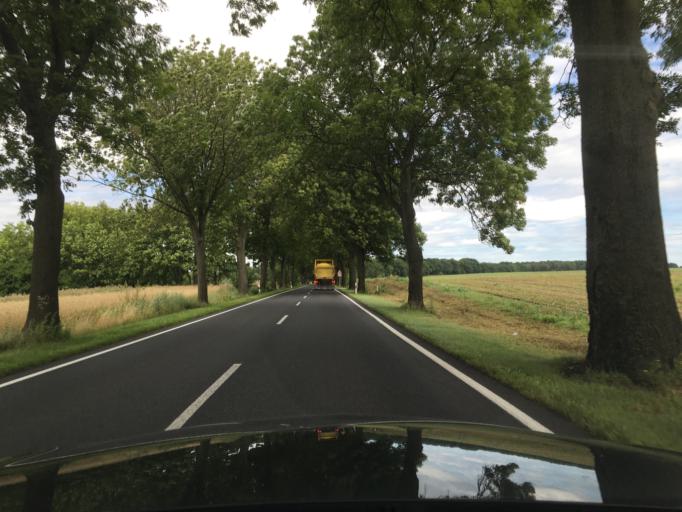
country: DE
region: Brandenburg
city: Gransee
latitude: 52.9066
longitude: 13.1578
